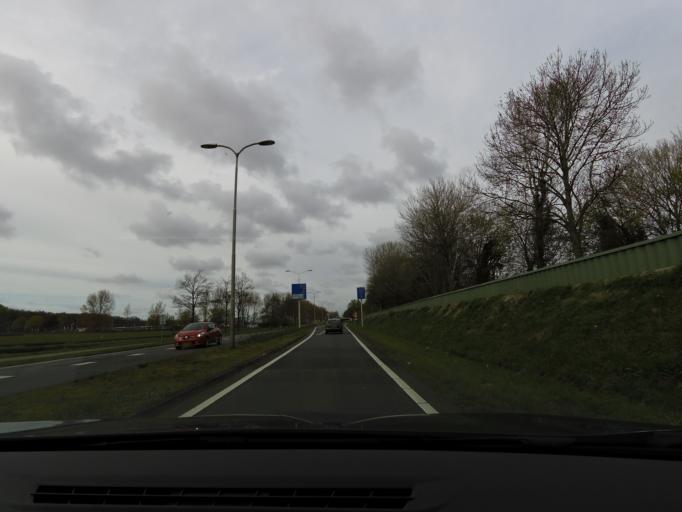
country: NL
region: South Holland
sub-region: Gemeente Lisse
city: Lisse
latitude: 52.2624
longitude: 4.5499
